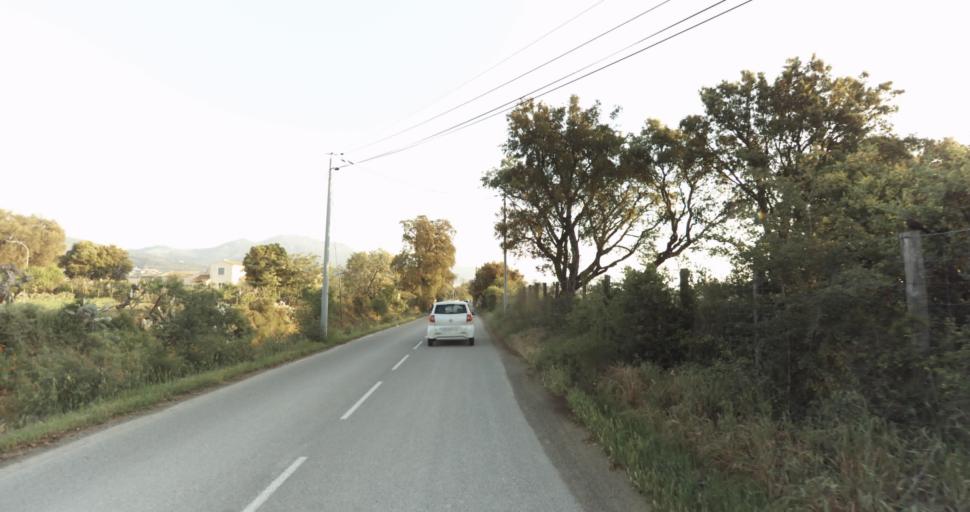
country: FR
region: Corsica
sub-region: Departement de la Haute-Corse
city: Biguglia
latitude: 42.6270
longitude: 9.4411
